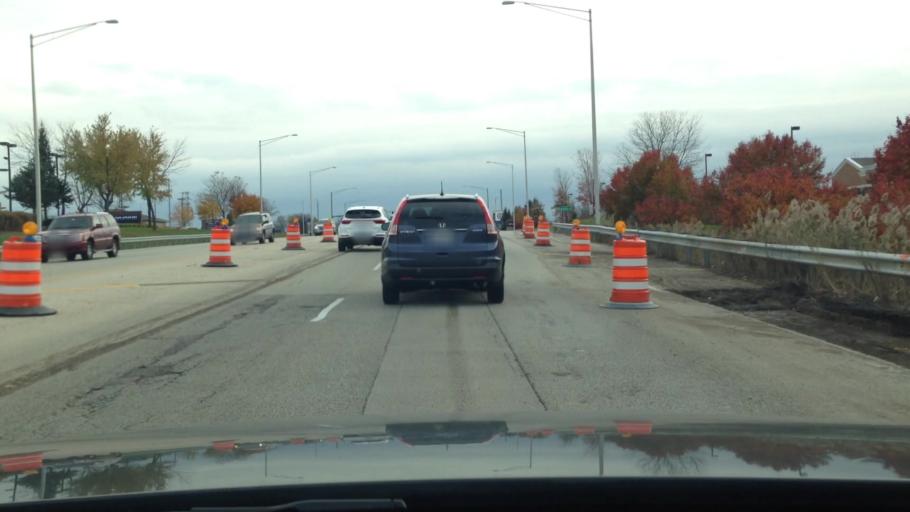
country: US
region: Illinois
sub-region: McHenry County
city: Lake in the Hills
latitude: 42.1639
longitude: -88.3355
